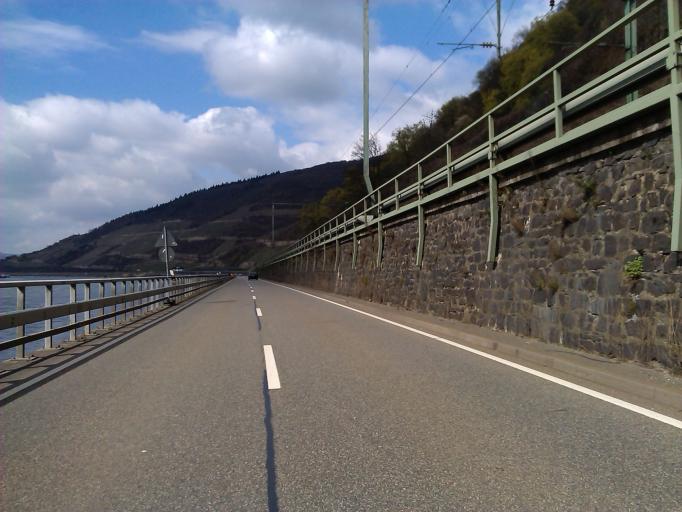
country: DE
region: Rheinland-Pfalz
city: Trechtingshausen
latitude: 50.0097
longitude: 7.8586
